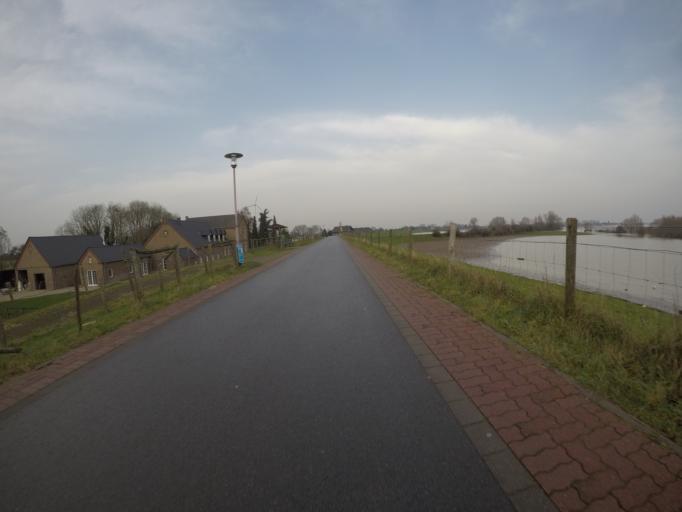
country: DE
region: North Rhine-Westphalia
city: Rees
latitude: 51.7175
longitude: 6.4036
